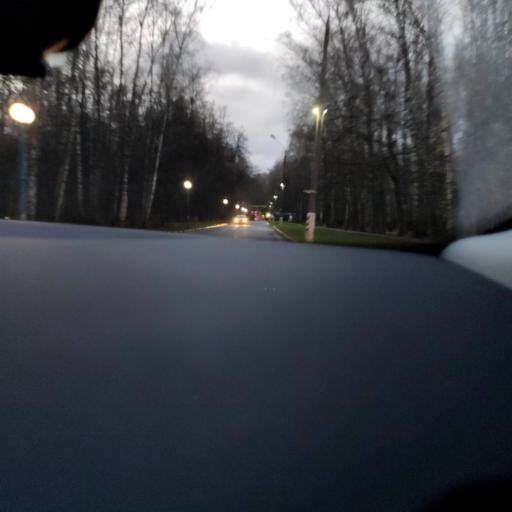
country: RU
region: Moskovskaya
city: Bogorodskoye
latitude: 55.8355
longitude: 37.7447
